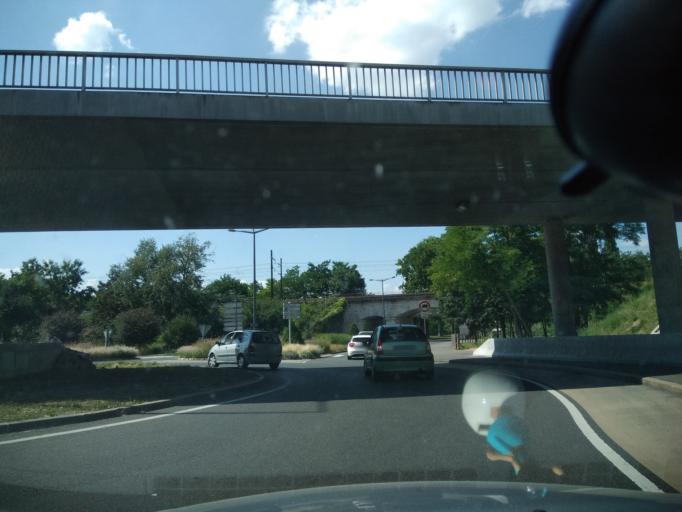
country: FR
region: Centre
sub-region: Departement d'Indre-et-Loire
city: Tours
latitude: 47.3638
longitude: 0.6999
